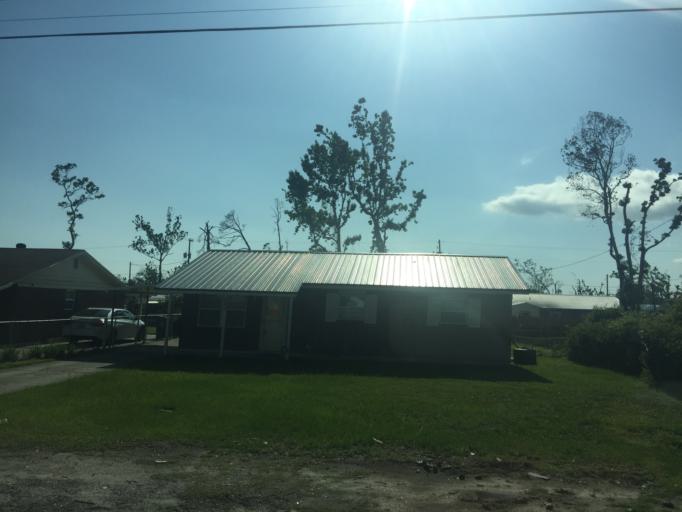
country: US
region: Florida
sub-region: Bay County
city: Springfield
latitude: 30.1630
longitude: -85.6165
